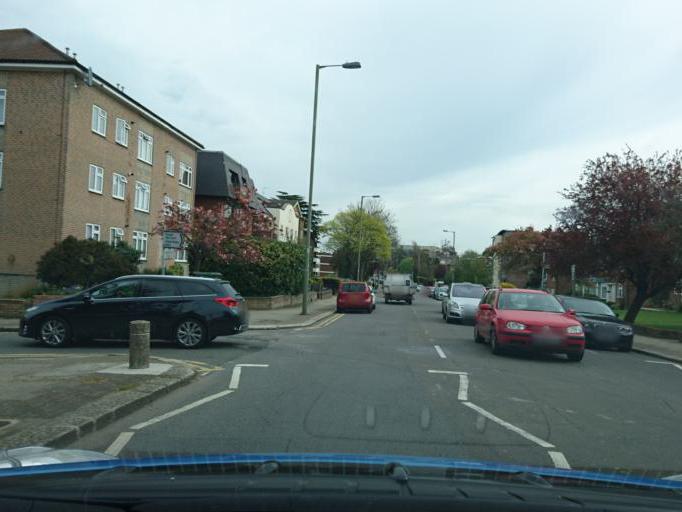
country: GB
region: England
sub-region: Greater London
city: Barnet
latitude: 51.6482
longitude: -0.1822
